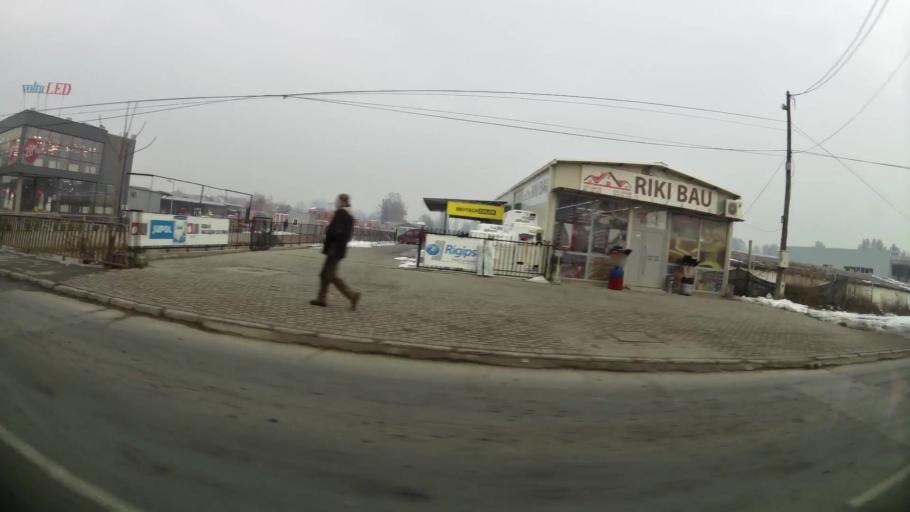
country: MK
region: Suto Orizari
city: Suto Orizare
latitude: 42.0265
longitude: 21.4295
